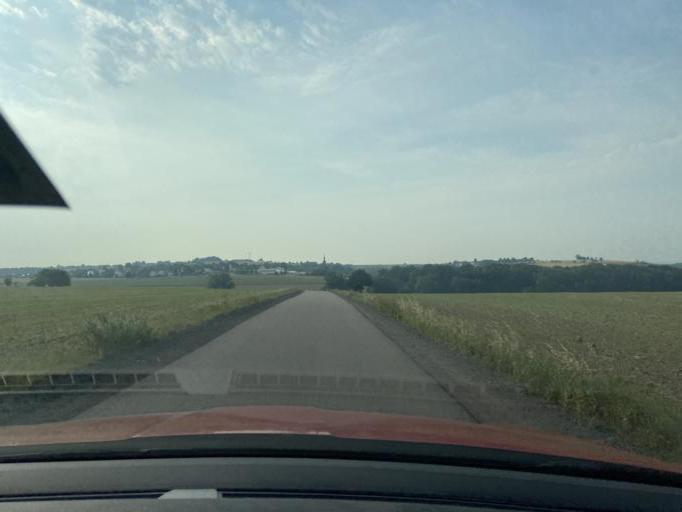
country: DE
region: Saxony
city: Tharandt
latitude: 51.0112
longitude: 13.5807
